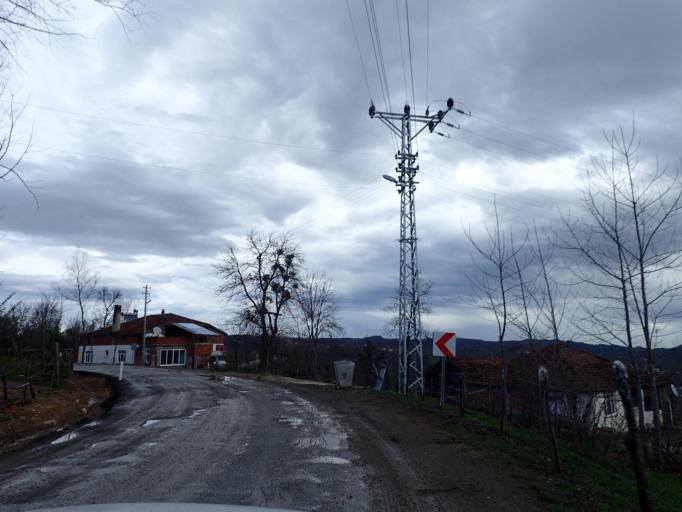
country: TR
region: Ordu
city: Kumru
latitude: 40.9308
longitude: 37.2597
